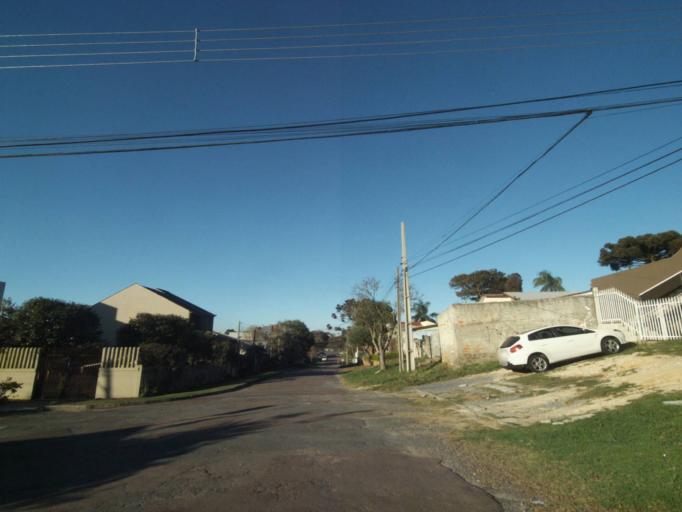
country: BR
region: Parana
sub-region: Curitiba
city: Curitiba
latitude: -25.3884
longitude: -49.2497
